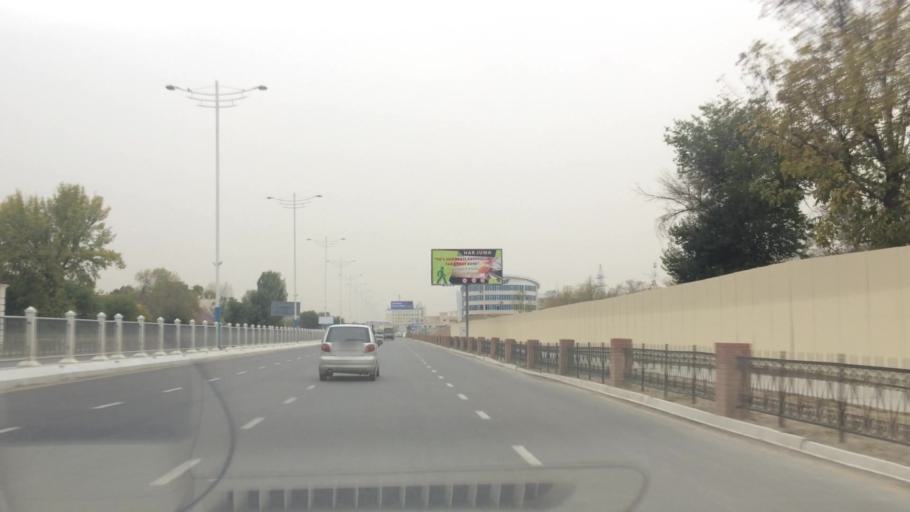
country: UZ
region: Toshkent
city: Salor
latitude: 41.3037
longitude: 69.3150
